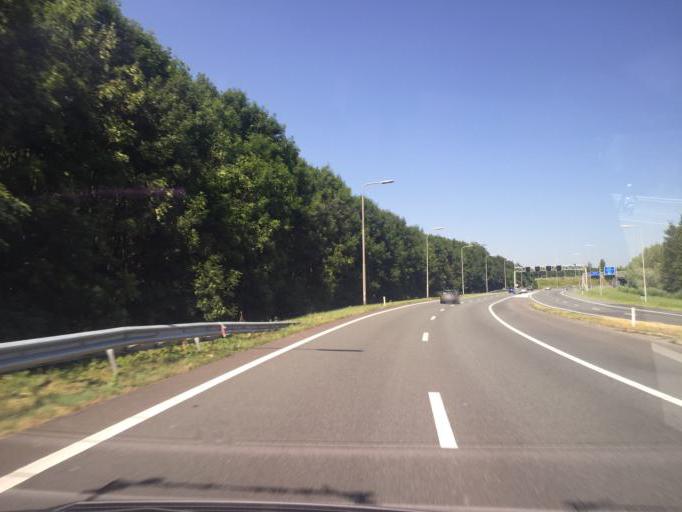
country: NL
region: Utrecht
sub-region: Gemeente Nieuwegein
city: Nieuwegein
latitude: 52.0650
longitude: 5.0758
